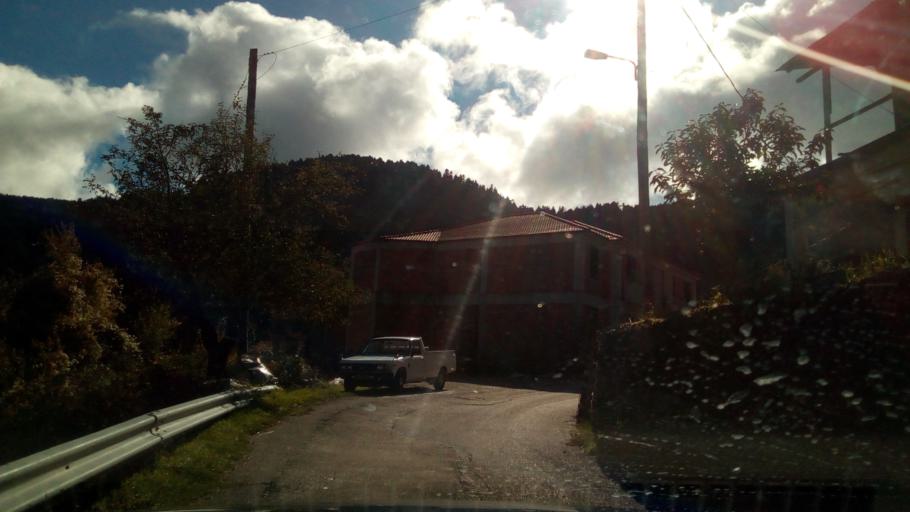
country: GR
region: West Greece
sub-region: Nomos Aitolias kai Akarnanias
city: Nafpaktos
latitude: 38.5900
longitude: 21.9255
